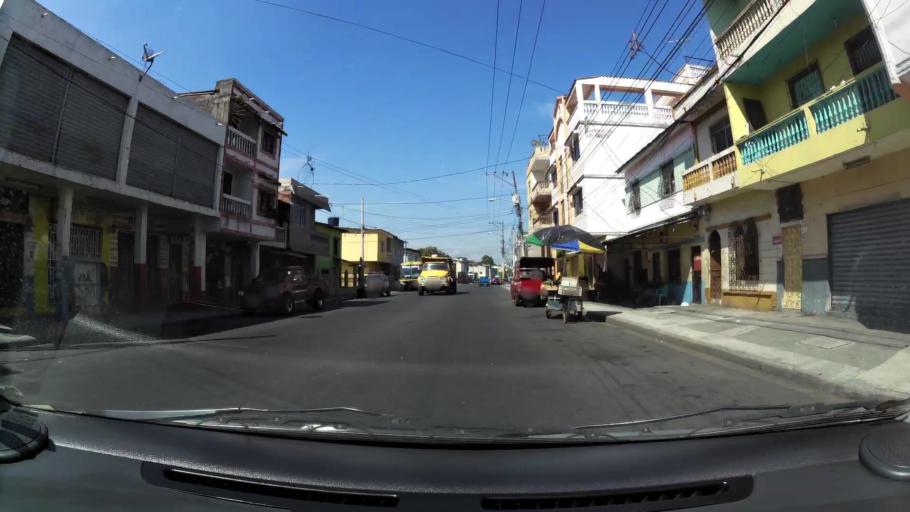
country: EC
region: Guayas
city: Guayaquil
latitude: -2.2105
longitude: -79.9068
